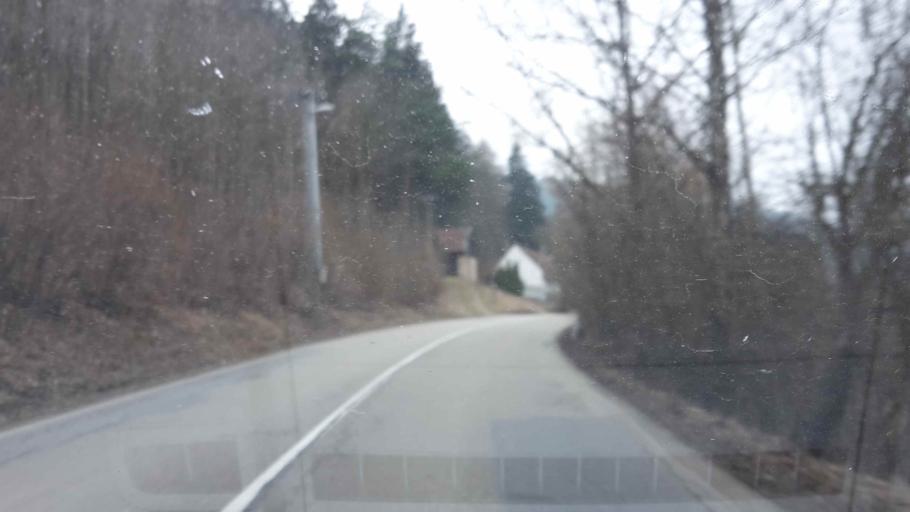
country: CZ
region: South Moravian
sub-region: Okres Brno-Venkov
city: Dolni Loucky
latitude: 49.3771
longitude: 16.3831
